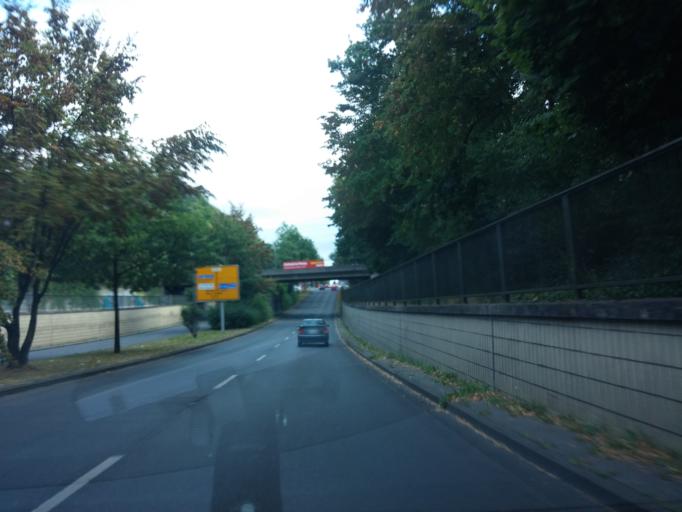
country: DE
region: North Rhine-Westphalia
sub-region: Regierungsbezirk Munster
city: Gladbeck
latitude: 51.5853
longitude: 7.0418
